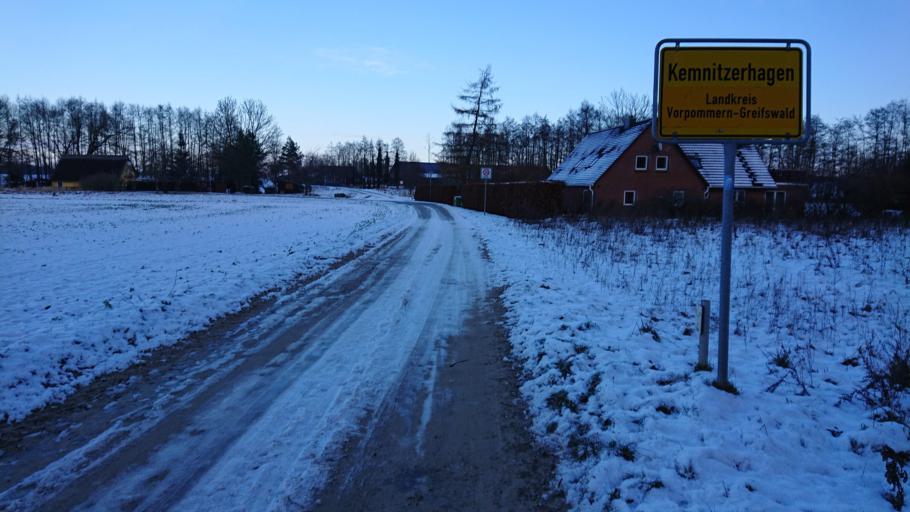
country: DE
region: Mecklenburg-Vorpommern
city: Kemnitz
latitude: 54.0608
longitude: 13.5465
